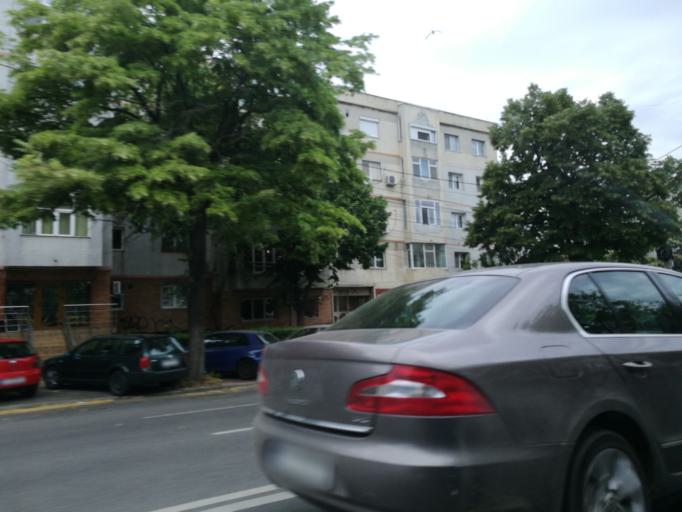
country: RO
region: Constanta
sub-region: Municipiul Constanta
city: Constanta
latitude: 44.1902
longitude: 28.6336
